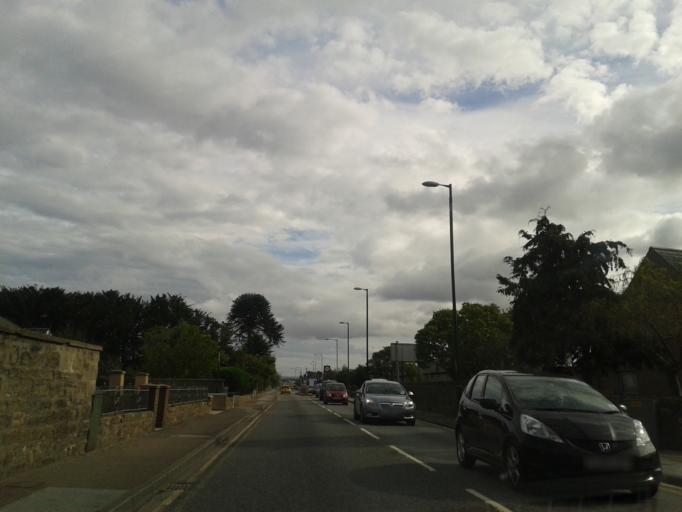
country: GB
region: Scotland
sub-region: Moray
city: Elgin
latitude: 57.6480
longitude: -3.3016
